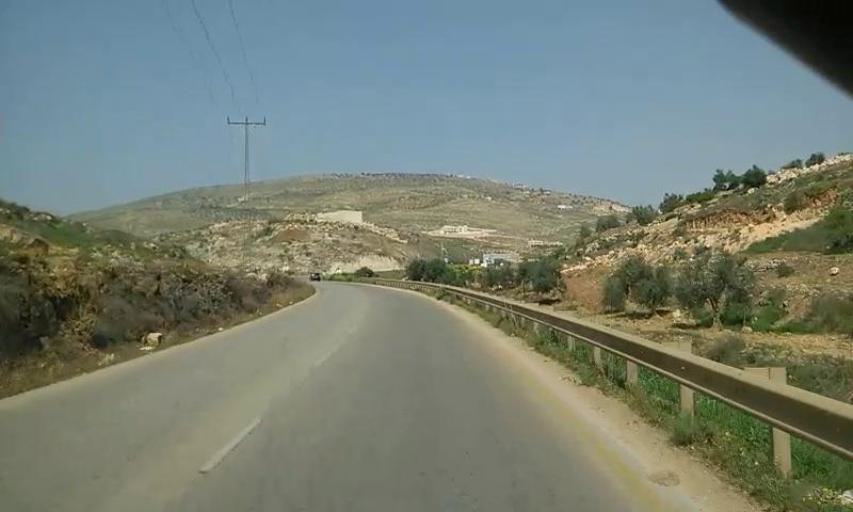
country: PS
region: West Bank
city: Tubas
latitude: 32.3009
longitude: 35.3645
